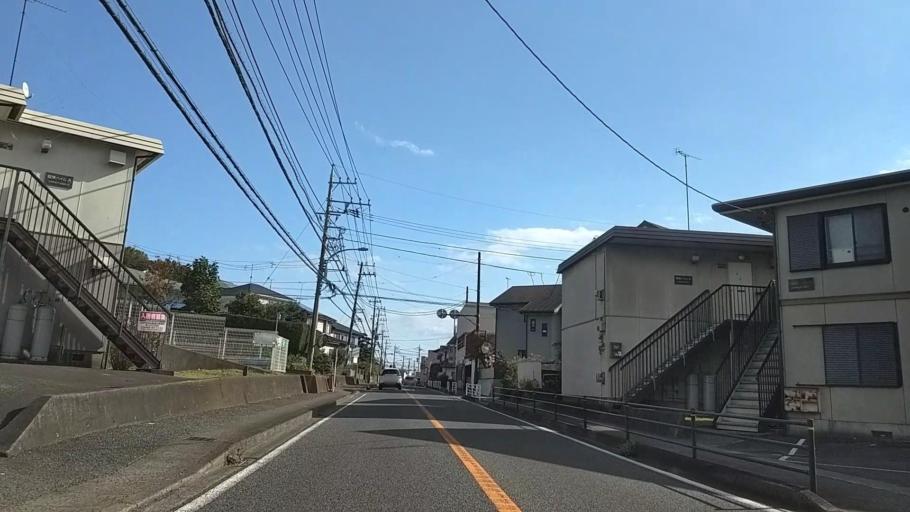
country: JP
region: Kanagawa
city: Odawara
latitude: 35.3261
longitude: 139.1601
